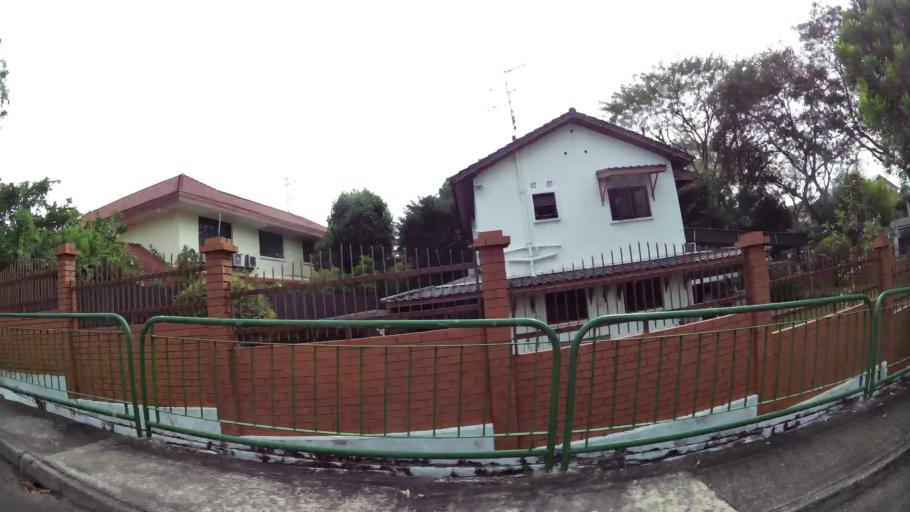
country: SG
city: Singapore
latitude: 1.3182
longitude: 103.7883
